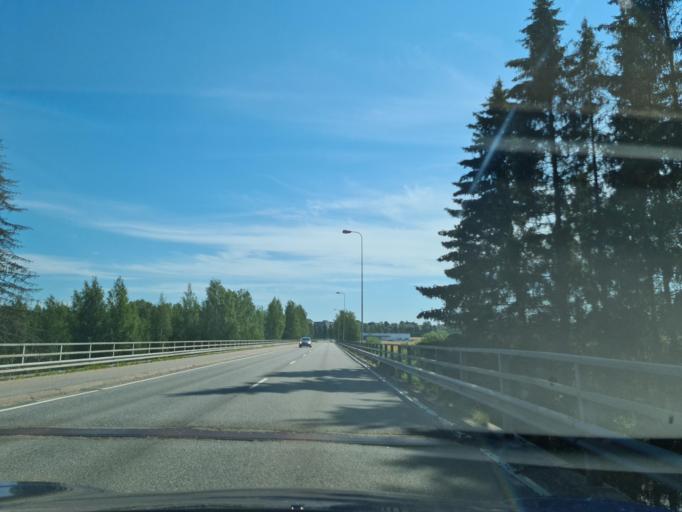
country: FI
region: Varsinais-Suomi
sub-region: Turku
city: Paimio
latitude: 60.4550
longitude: 22.6751
